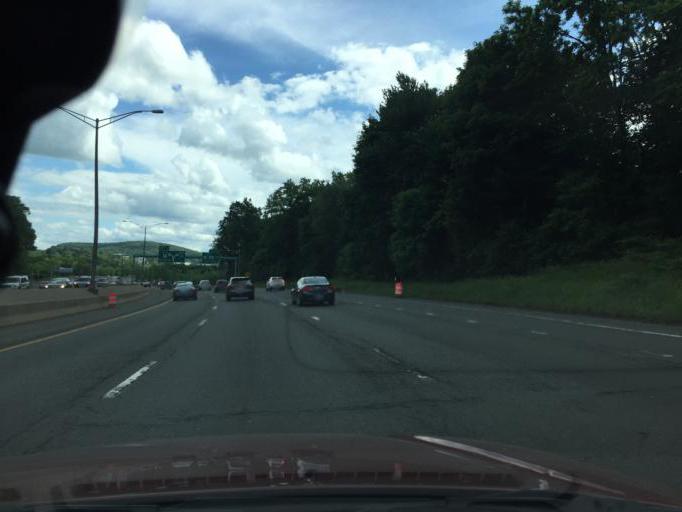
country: US
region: Connecticut
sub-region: Fairfield County
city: Danbury
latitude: 41.3937
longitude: -73.4784
